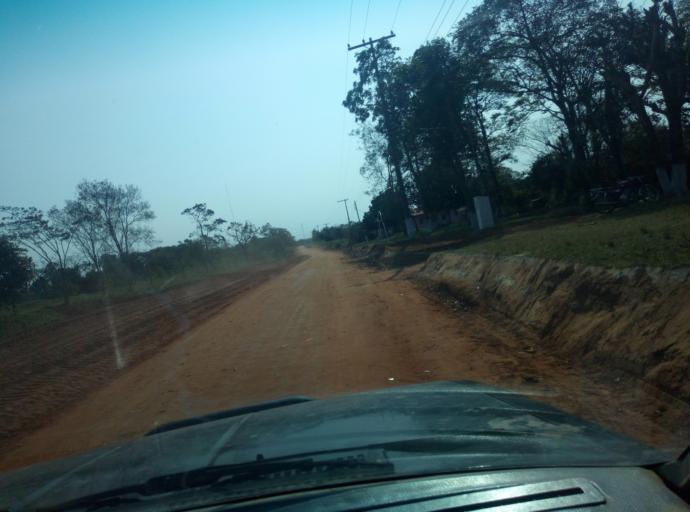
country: PY
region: Caaguazu
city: Carayao
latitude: -25.3266
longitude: -56.3304
